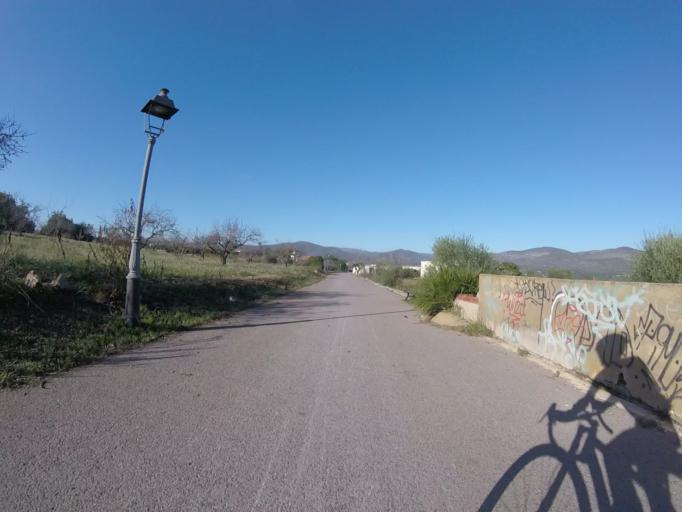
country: ES
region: Valencia
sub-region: Provincia de Castello
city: Santa Magdalena de Pulpis
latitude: 40.3552
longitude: 0.3072
